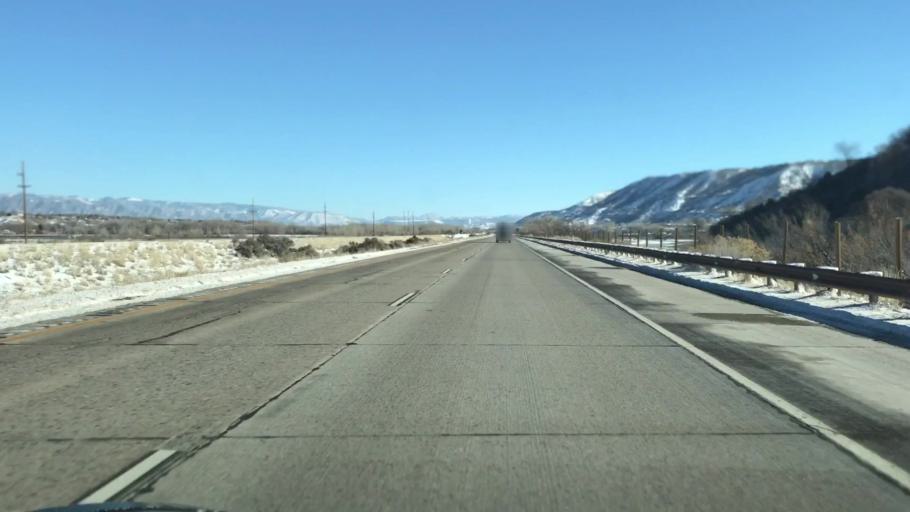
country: US
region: Colorado
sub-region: Garfield County
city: Rifle
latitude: 39.5199
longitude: -107.8211
